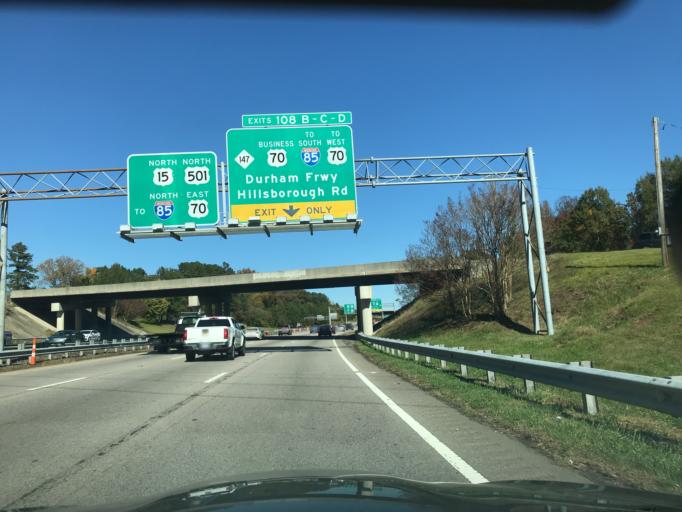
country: US
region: North Carolina
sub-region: Durham County
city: Durham
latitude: 36.0111
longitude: -78.9555
